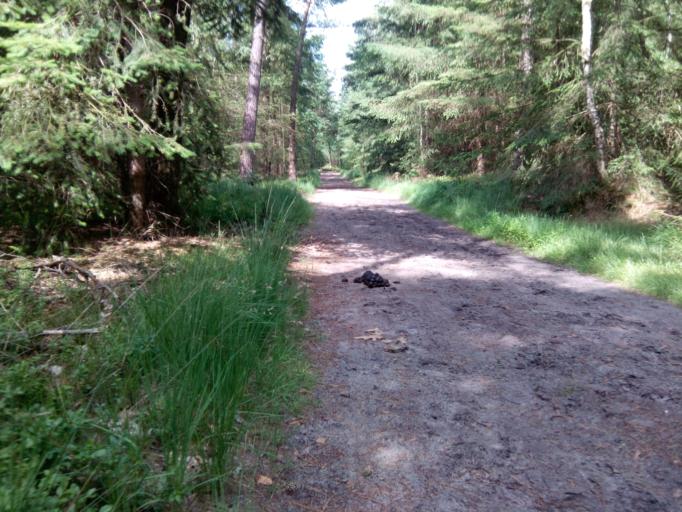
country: NL
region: Utrecht
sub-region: Gemeente Utrechtse Heuvelrug
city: Maarn
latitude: 52.0908
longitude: 5.3672
